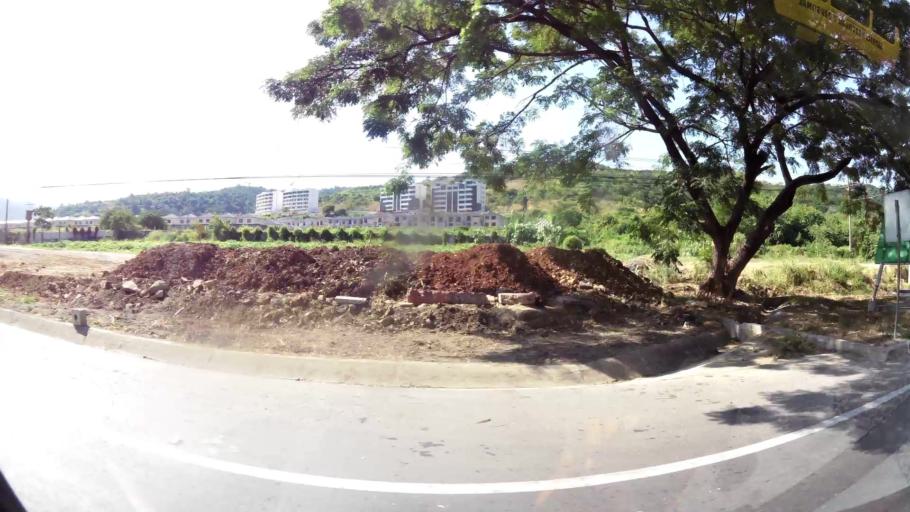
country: EC
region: Guayas
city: Santa Lucia
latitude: -2.1859
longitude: -79.9665
